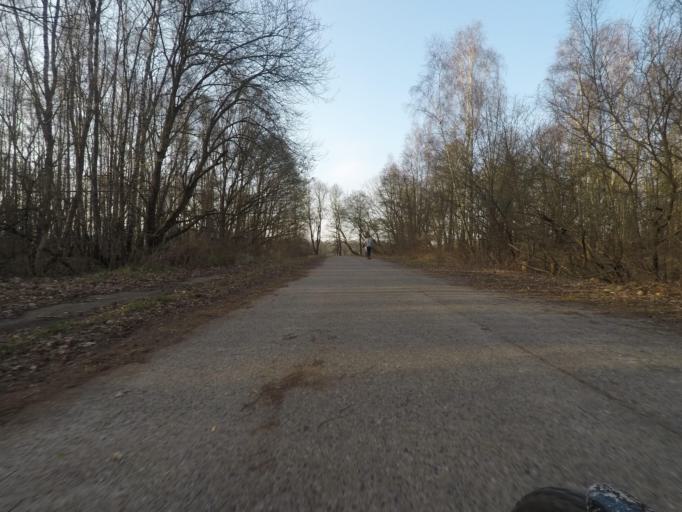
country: DE
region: Schleswig-Holstein
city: Stapelfeld
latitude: 53.6274
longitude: 10.1969
